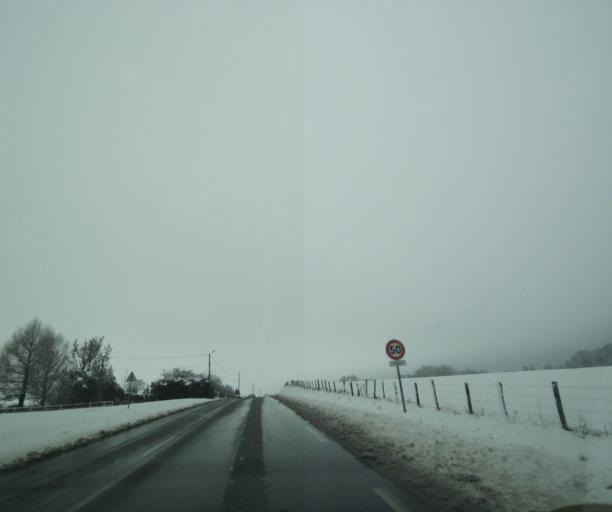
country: FR
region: Champagne-Ardenne
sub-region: Departement de la Haute-Marne
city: Montier-en-Der
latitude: 48.5381
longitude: 4.8216
